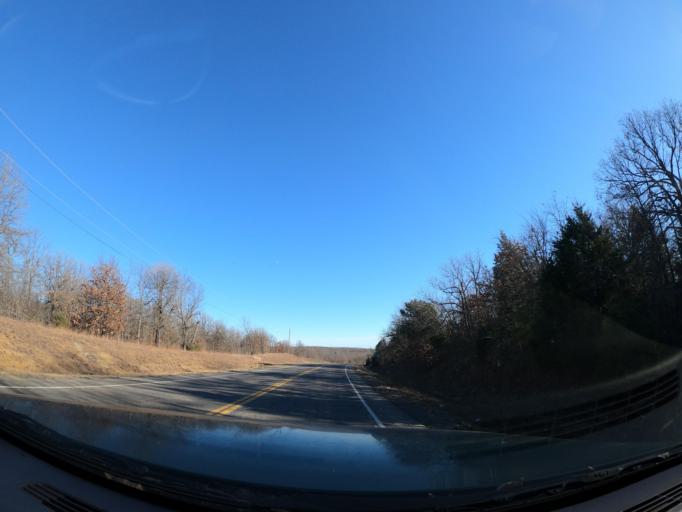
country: US
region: Oklahoma
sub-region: Pittsburg County
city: Longtown
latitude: 35.2241
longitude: -95.4322
